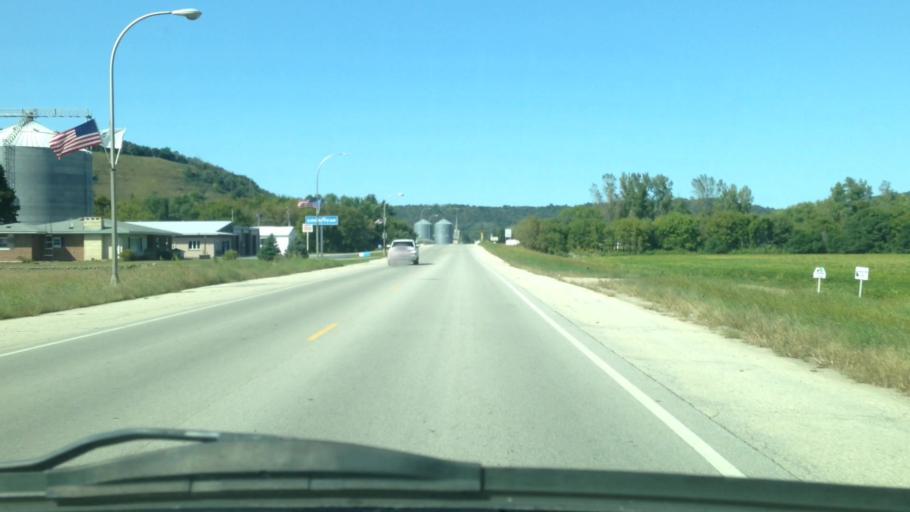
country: US
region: Minnesota
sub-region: Fillmore County
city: Rushford
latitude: 43.8007
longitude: -91.7531
